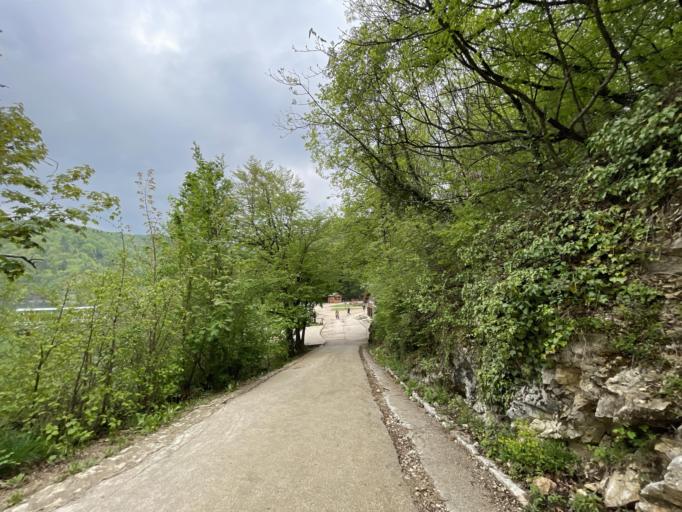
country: HR
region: Licko-Senjska
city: Jezerce
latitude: 44.8941
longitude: 15.6043
